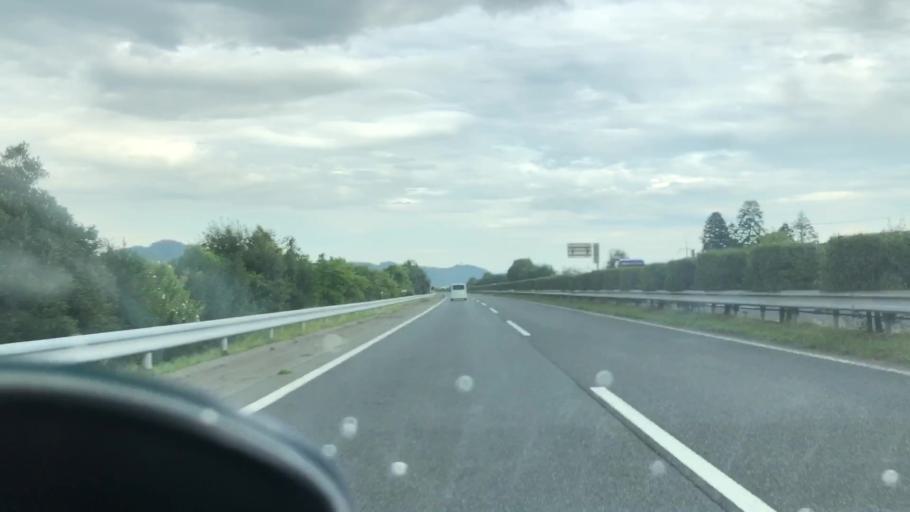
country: JP
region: Hyogo
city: Ono
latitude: 34.9436
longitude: 134.8112
